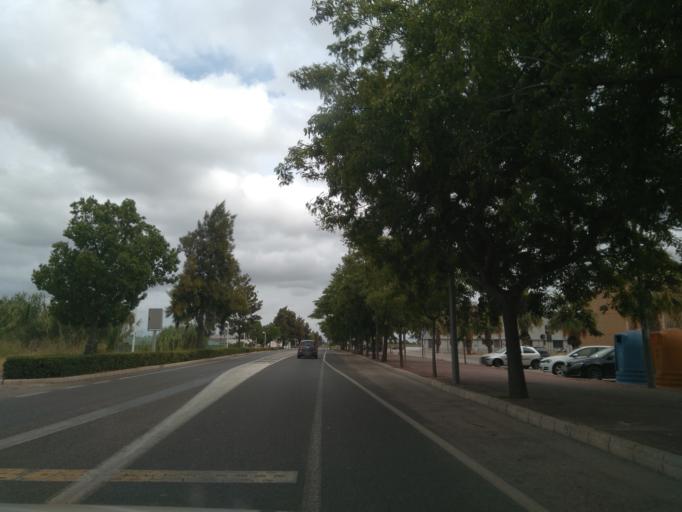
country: ES
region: Valencia
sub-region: Provincia de Valencia
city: Carlet
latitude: 39.2198
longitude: -0.5177
